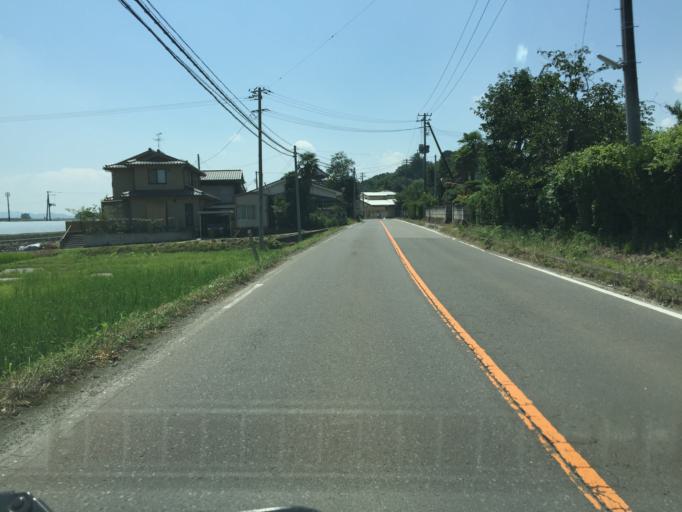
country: JP
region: Fukushima
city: Yanagawamachi-saiwaicho
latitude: 37.8771
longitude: 140.6130
